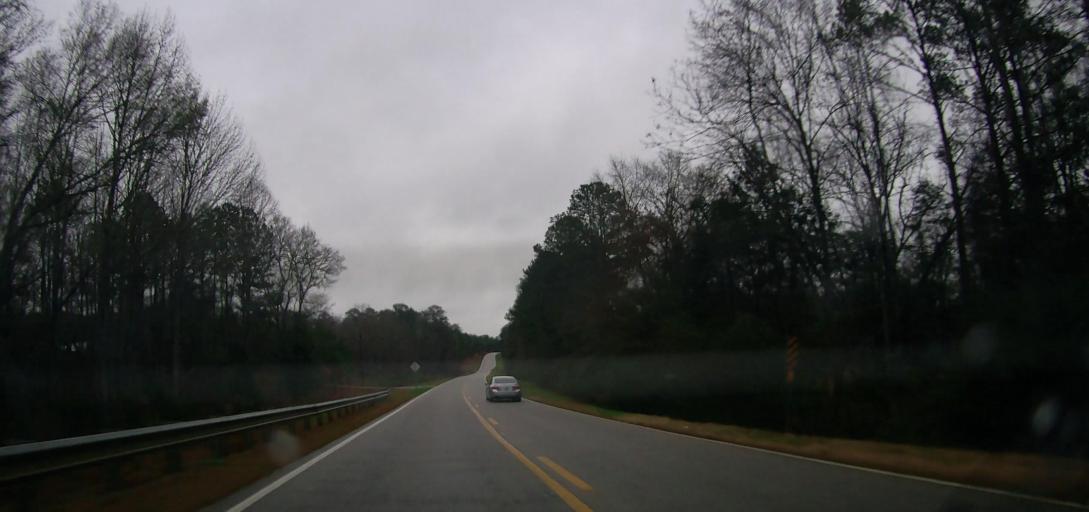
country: US
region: Alabama
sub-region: Bibb County
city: Centreville
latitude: 32.9046
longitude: -87.0063
